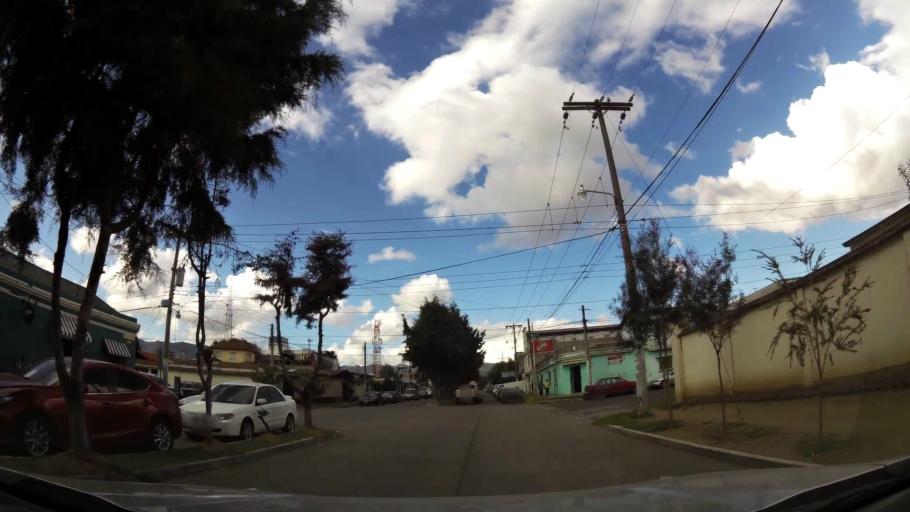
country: GT
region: Quetzaltenango
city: Quetzaltenango
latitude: 14.8457
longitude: -91.5259
